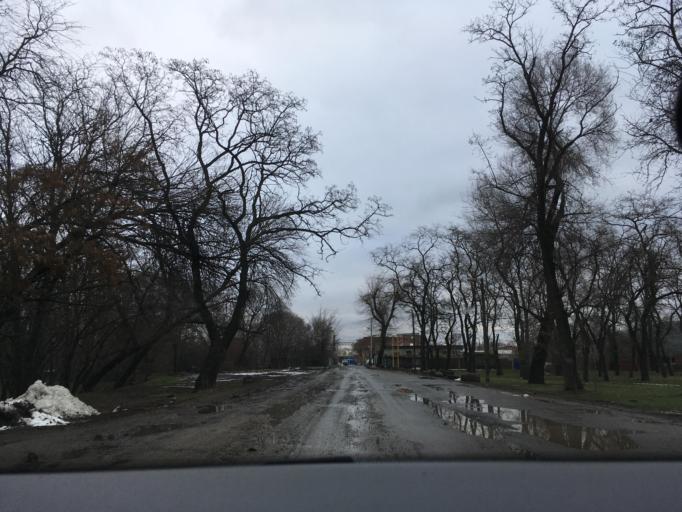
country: RU
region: Rostov
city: Rostov-na-Donu
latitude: 47.2111
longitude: 39.7167
